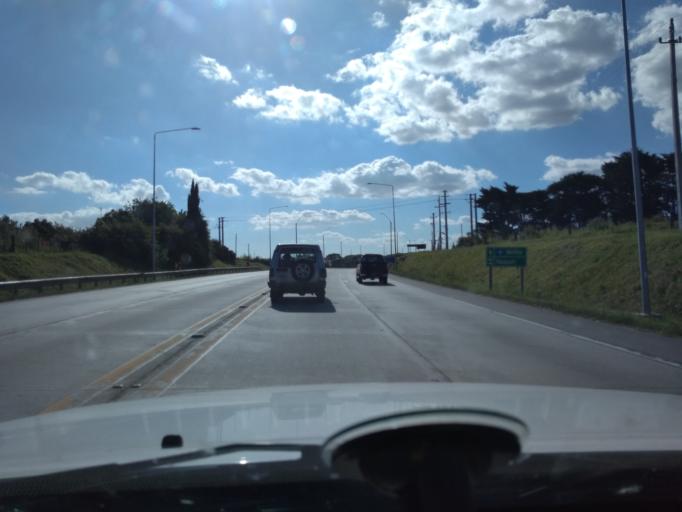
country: UY
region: Canelones
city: La Paz
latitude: -34.7832
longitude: -56.2490
